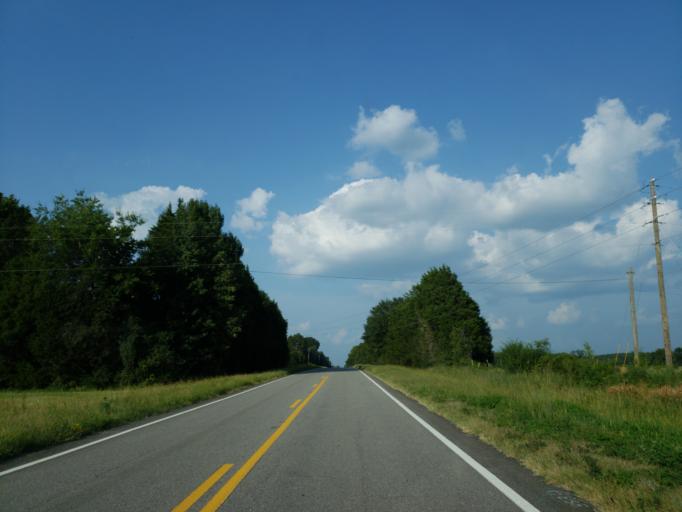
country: US
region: Alabama
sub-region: Greene County
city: Eutaw
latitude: 32.7646
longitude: -88.0037
